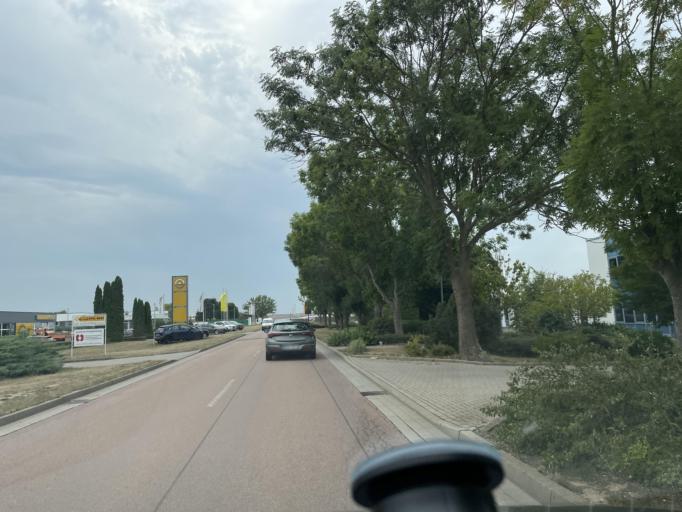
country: DE
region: Saxony-Anhalt
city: Calbe
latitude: 51.8986
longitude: 11.7567
